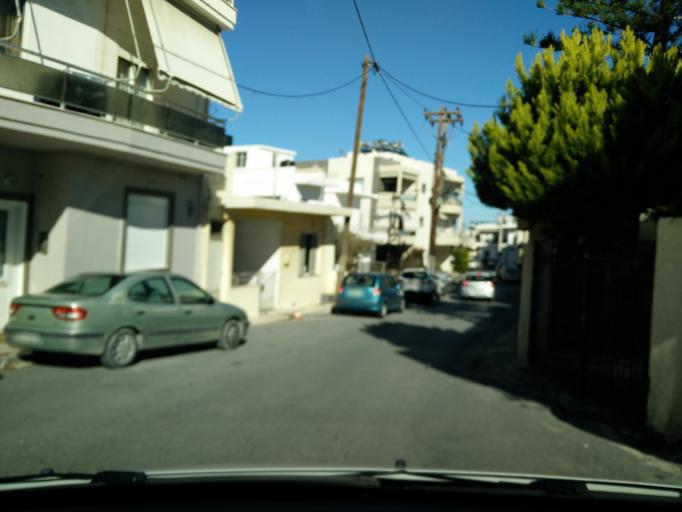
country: GR
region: Crete
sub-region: Nomos Irakleiou
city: Nea Alikarnassos
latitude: 35.3379
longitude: 25.1493
